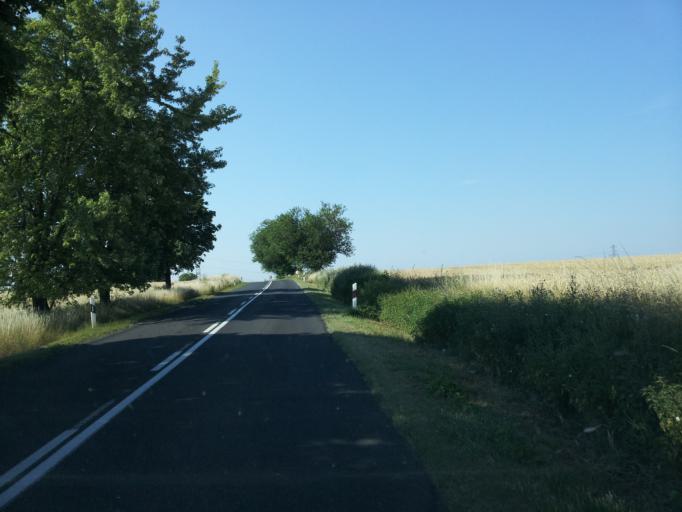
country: HU
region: Fejer
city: Lovasbereny
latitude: 47.4012
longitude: 18.5855
